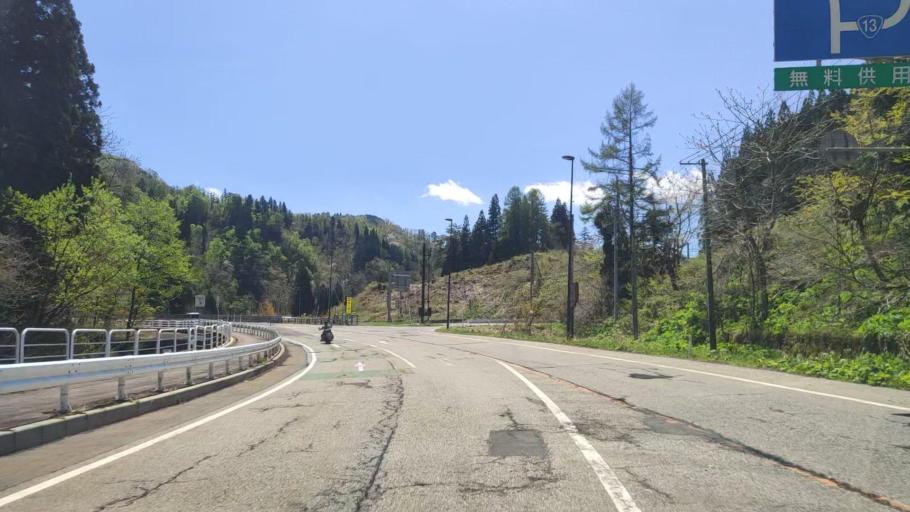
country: JP
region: Akita
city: Yuzawa
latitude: 38.9827
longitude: 140.3622
